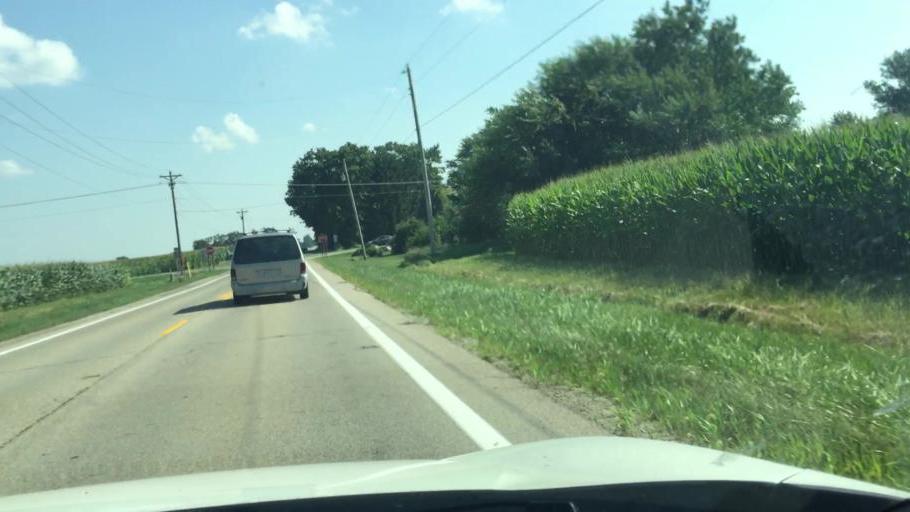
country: US
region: Ohio
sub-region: Champaign County
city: Mechanicsburg
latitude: 40.1436
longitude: -83.5295
